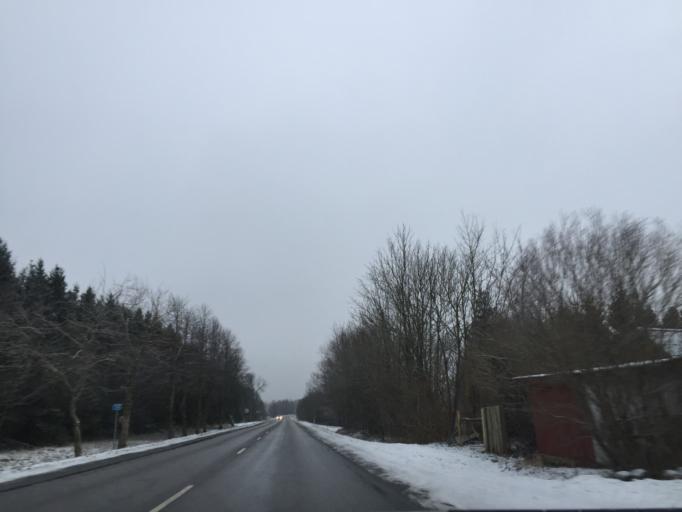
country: EE
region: Laeaene
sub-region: Lihula vald
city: Lihula
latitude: 58.5658
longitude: 23.9870
